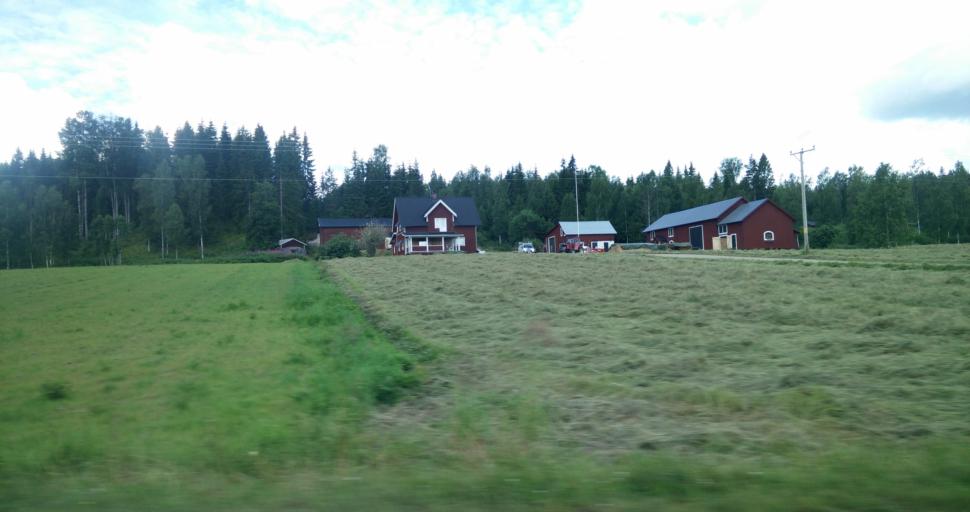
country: SE
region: Vaermland
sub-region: Hagfors Kommun
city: Ekshaerad
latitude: 60.1218
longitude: 13.4531
